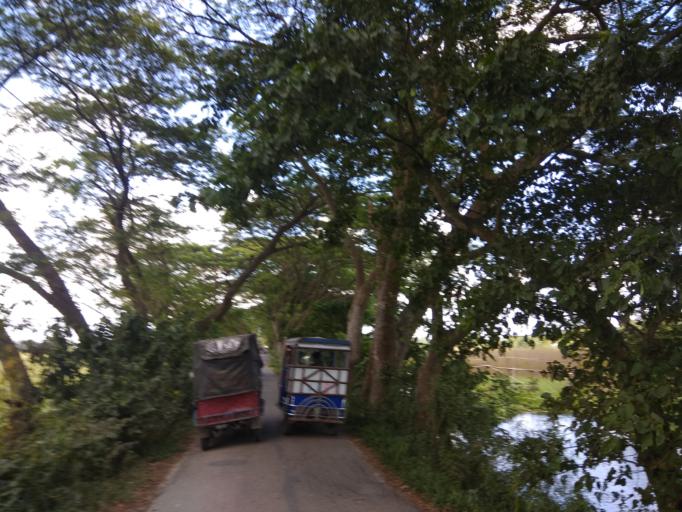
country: BD
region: Dhaka
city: Narayanganj
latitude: 23.4641
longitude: 90.4538
